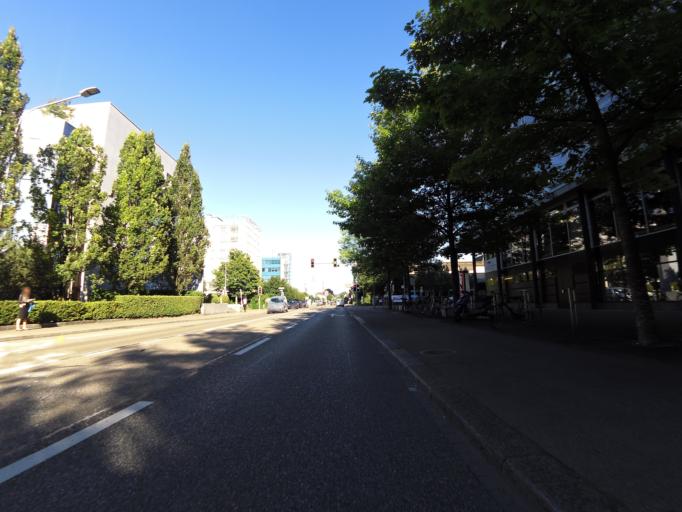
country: CH
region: Zurich
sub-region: Bezirk Zuerich
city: Zuerich (Kreis 9) / Altstetten
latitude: 47.3866
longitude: 8.4957
